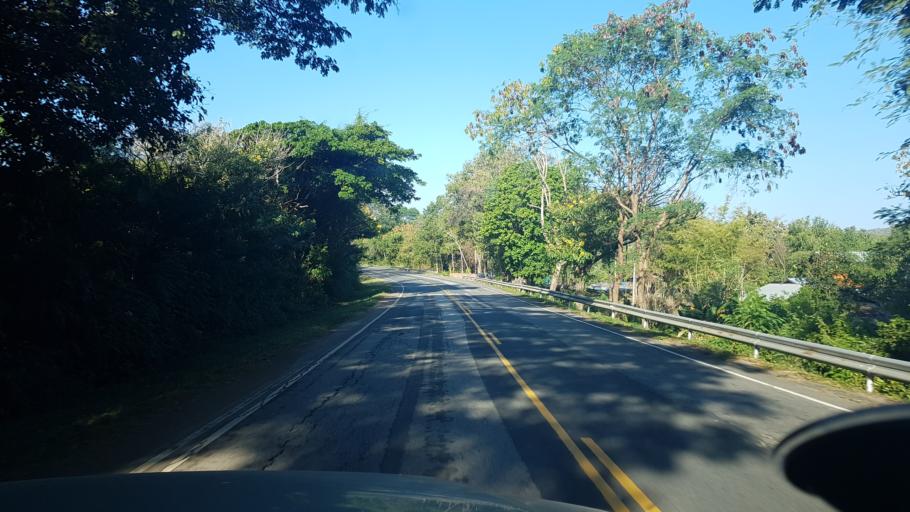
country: TH
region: Phetchabun
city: Lom Sak
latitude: 16.7371
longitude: 101.4273
